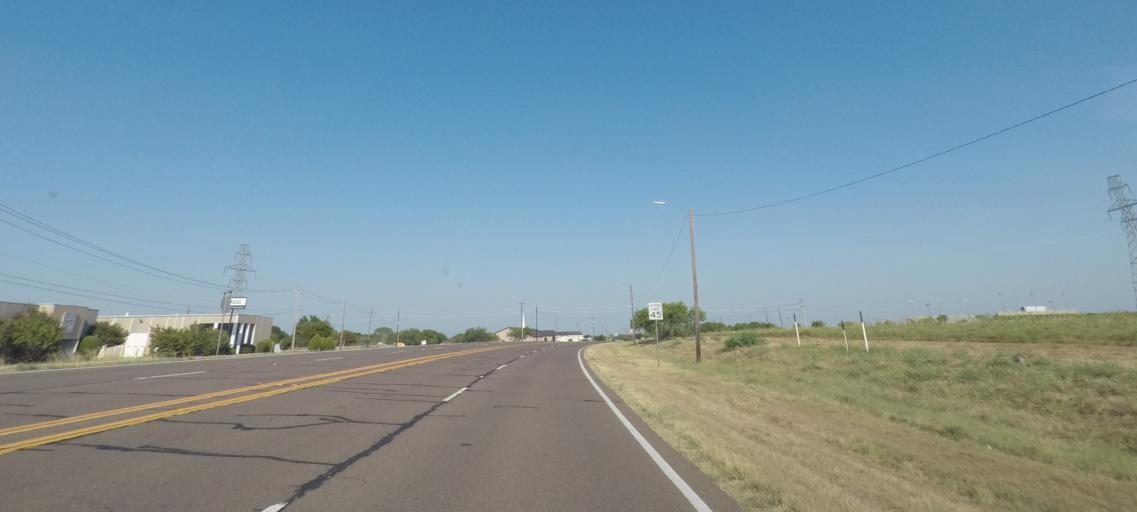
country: US
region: Texas
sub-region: Wichita County
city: Wichita Falls
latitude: 33.8592
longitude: -98.5891
